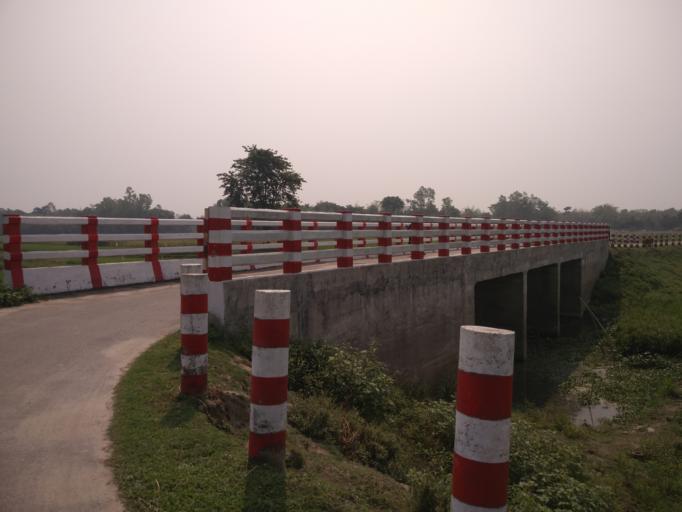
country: BD
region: Dhaka
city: Muktagacha
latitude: 24.9026
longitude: 90.2586
